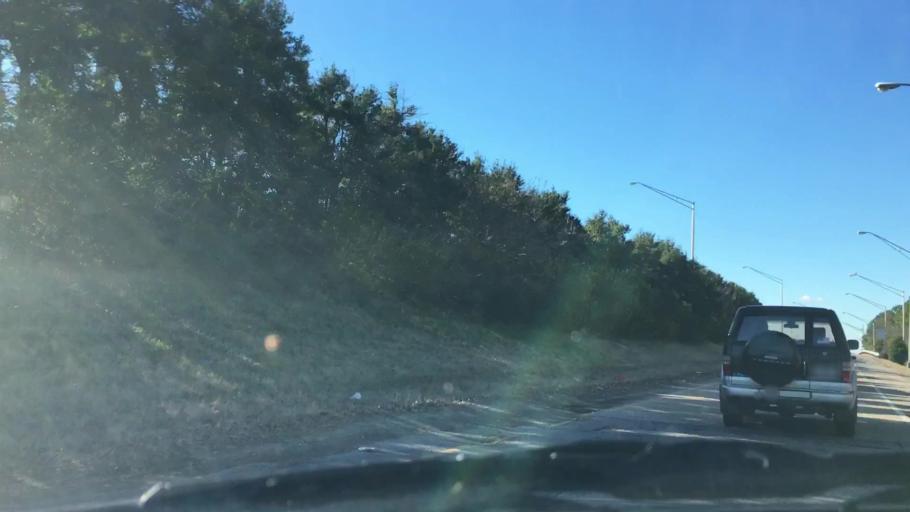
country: US
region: Virginia
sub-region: City of Virginia Beach
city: Virginia Beach
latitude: 36.8460
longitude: -76.0211
